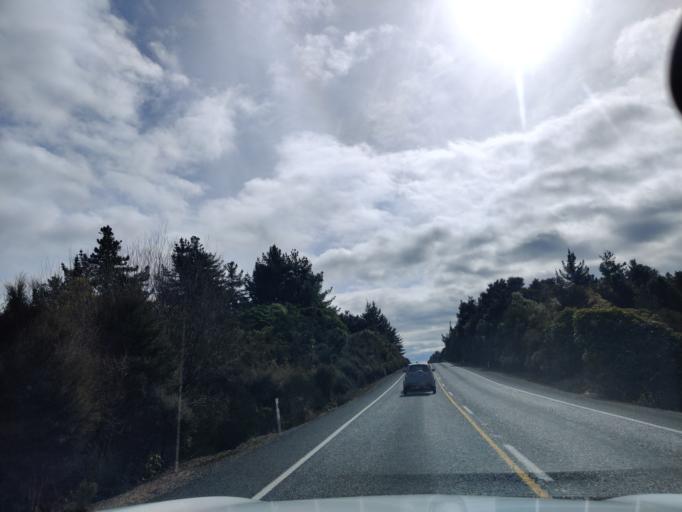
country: NZ
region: Waikato
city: Turangi
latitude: -39.0266
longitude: 175.8102
